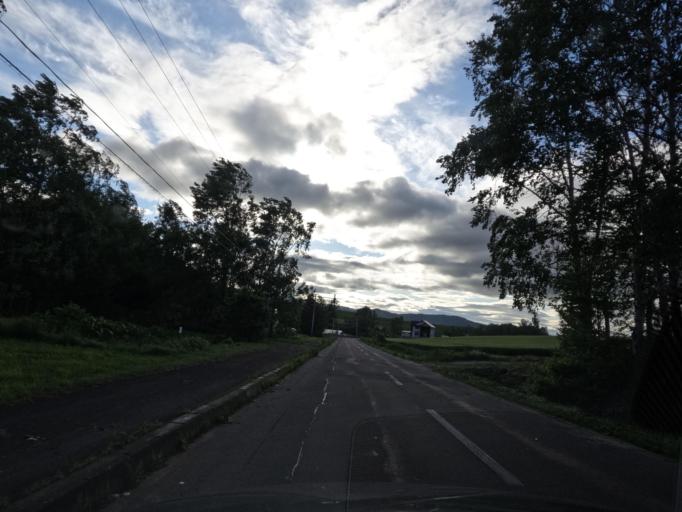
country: JP
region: Hokkaido
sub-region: Asahikawa-shi
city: Asahikawa
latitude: 43.6303
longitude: 142.4383
